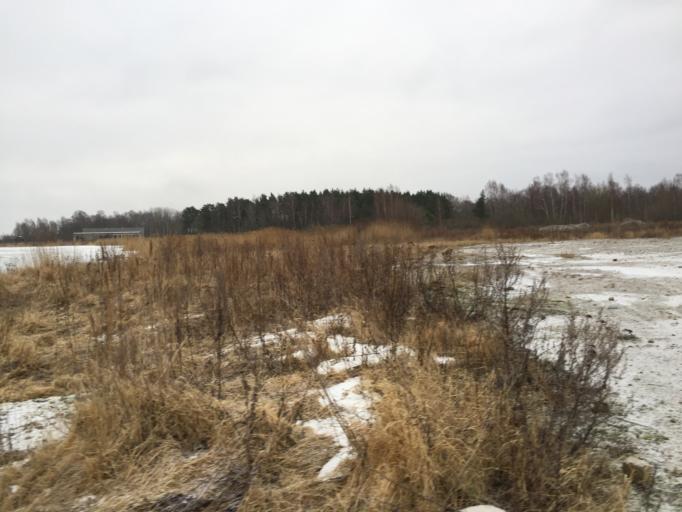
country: EE
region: Saare
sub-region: Orissaare vald
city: Orissaare
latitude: 58.6835
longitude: 23.1939
